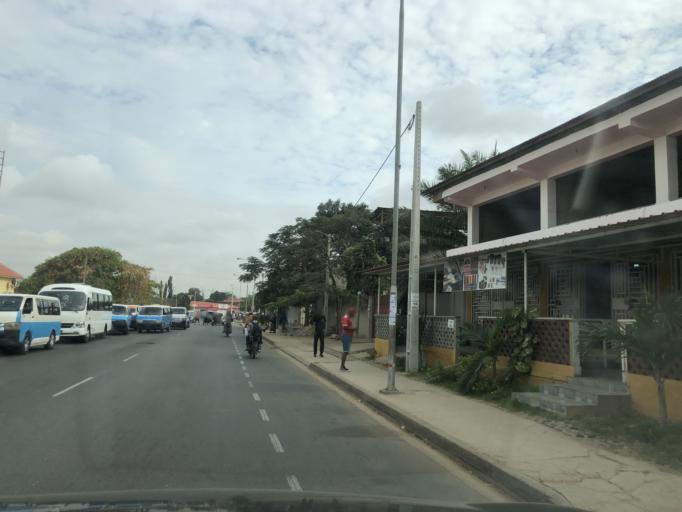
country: AO
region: Luanda
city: Luanda
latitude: -8.9135
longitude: 13.3719
